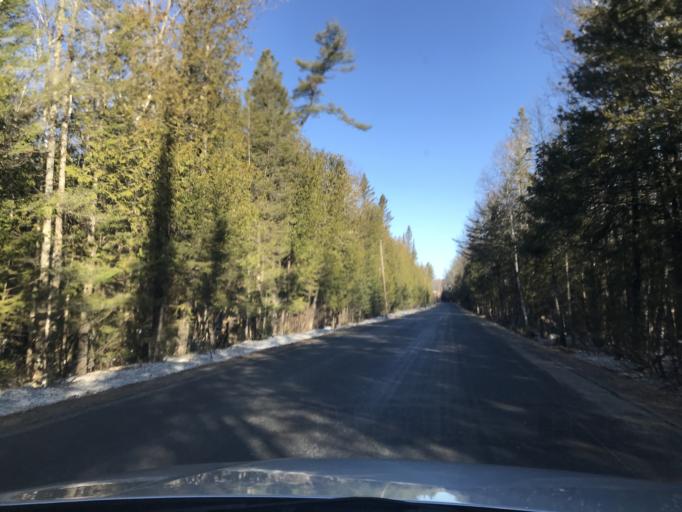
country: US
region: Wisconsin
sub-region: Marinette County
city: Niagara
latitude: 45.3769
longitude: -88.0229
